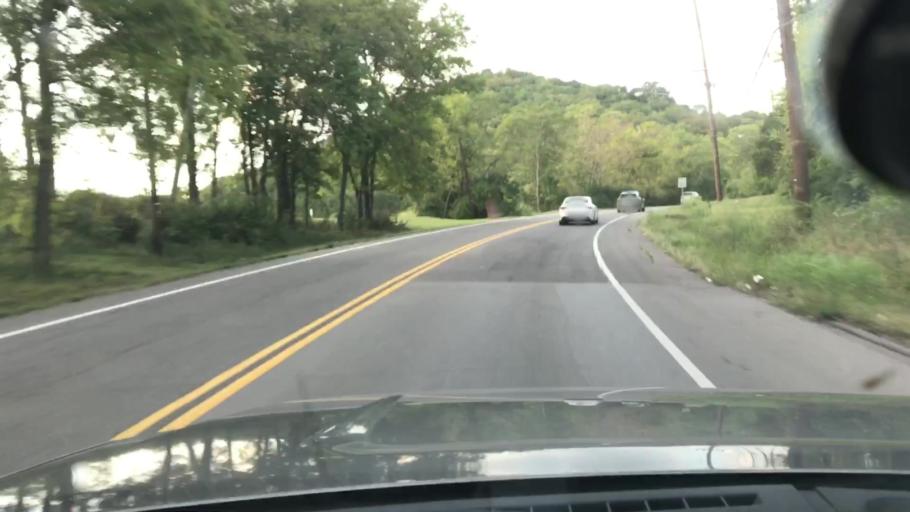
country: US
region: Tennessee
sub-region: Davidson County
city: Nashville
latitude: 36.2232
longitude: -86.8381
